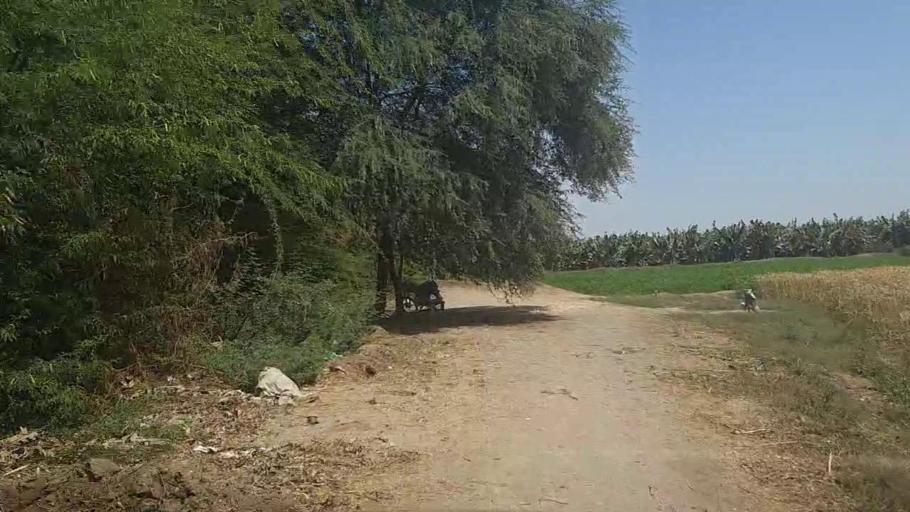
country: PK
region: Sindh
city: Thatta
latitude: 24.7914
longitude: 68.0152
